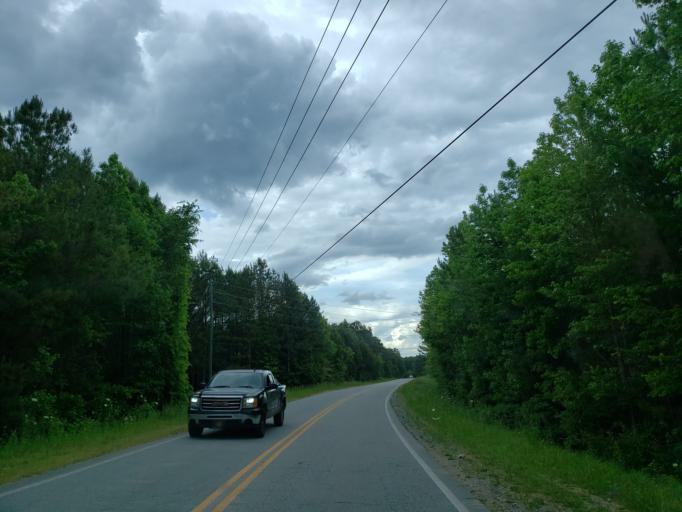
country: US
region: Georgia
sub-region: Polk County
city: Rockmart
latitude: 33.9084
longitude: -85.0650
